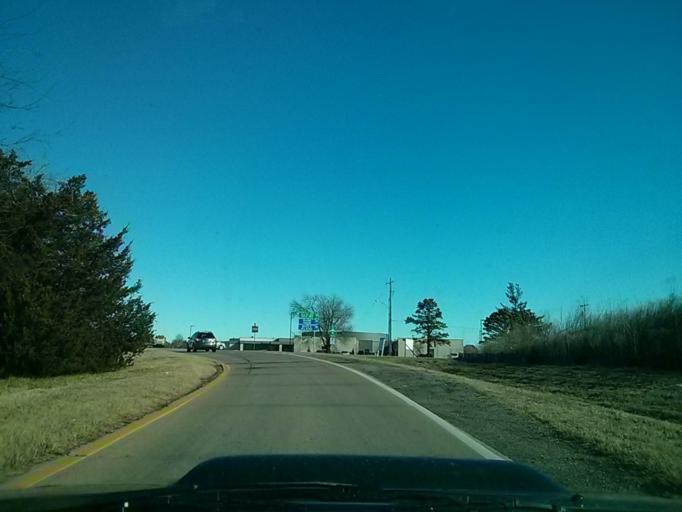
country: US
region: Oklahoma
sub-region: Tulsa County
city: Jenks
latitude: 36.0240
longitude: -96.0109
